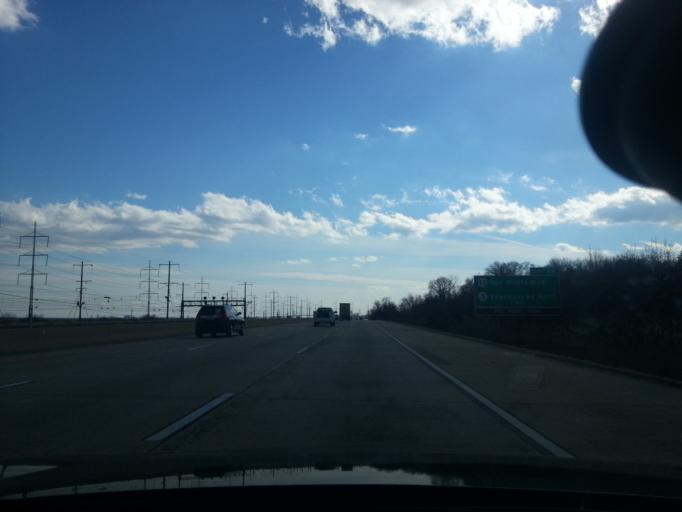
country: US
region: Delaware
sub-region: New Castle County
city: Edgemoor
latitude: 39.7662
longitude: -75.4861
